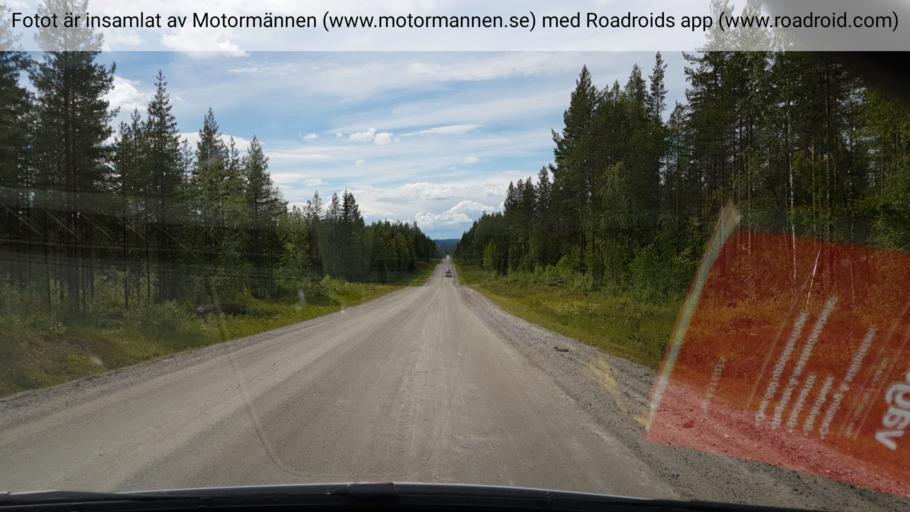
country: SE
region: Vaesternorrland
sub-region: Solleftea Kommun
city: Solleftea
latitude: 63.3182
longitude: 17.3165
